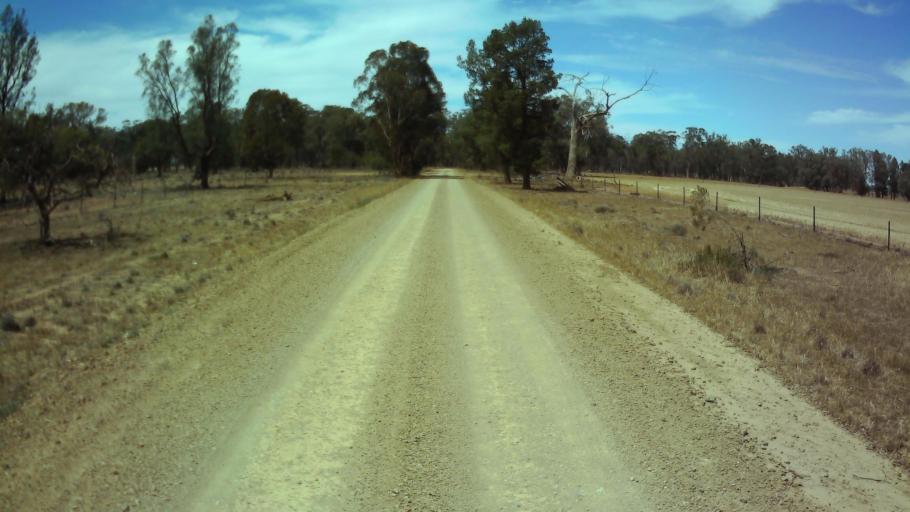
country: AU
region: New South Wales
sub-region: Weddin
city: Grenfell
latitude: -33.8549
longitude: 147.8054
